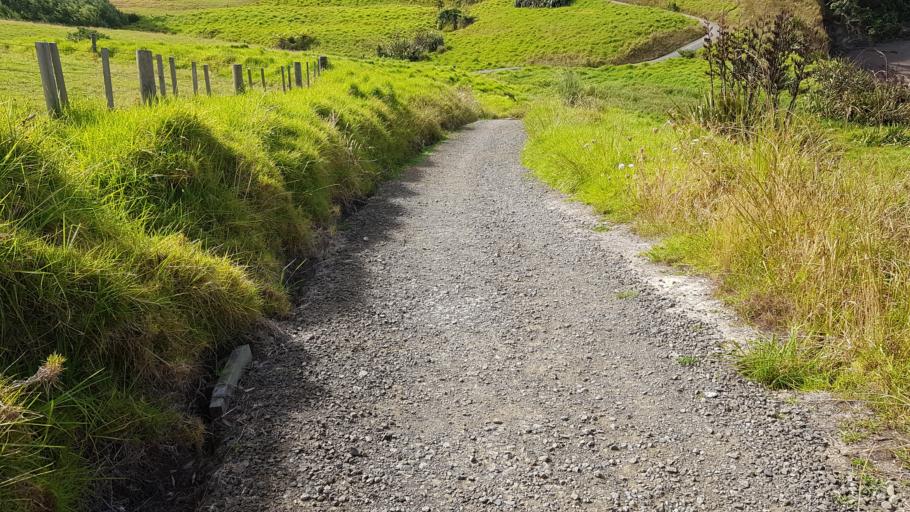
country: NZ
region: Auckland
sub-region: Auckland
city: Rothesay Bay
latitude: -36.6686
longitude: 174.7461
